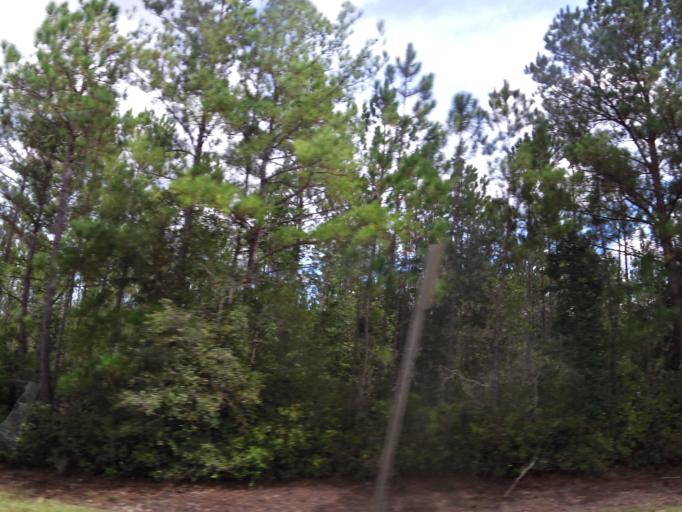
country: US
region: Georgia
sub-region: Brantley County
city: Nahunta
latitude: 31.1877
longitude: -81.9867
